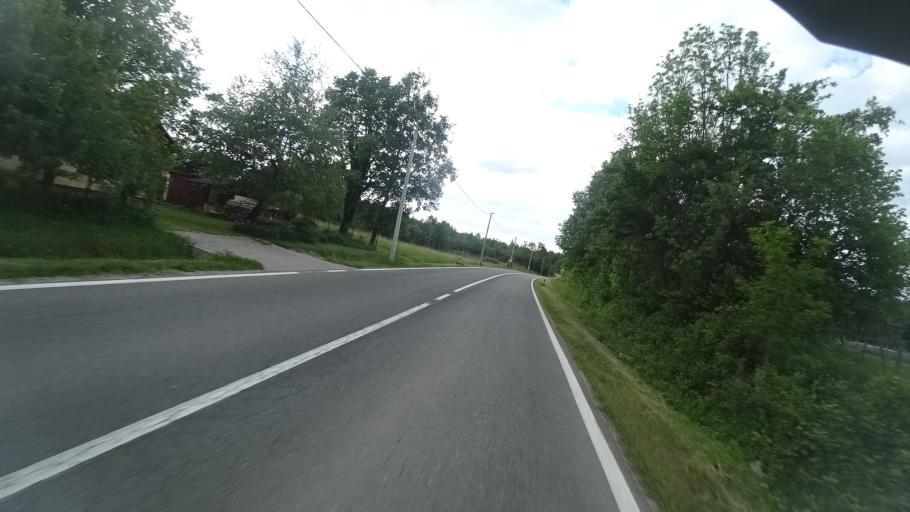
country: HR
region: Licko-Senjska
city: Gospic
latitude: 44.4922
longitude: 15.4604
